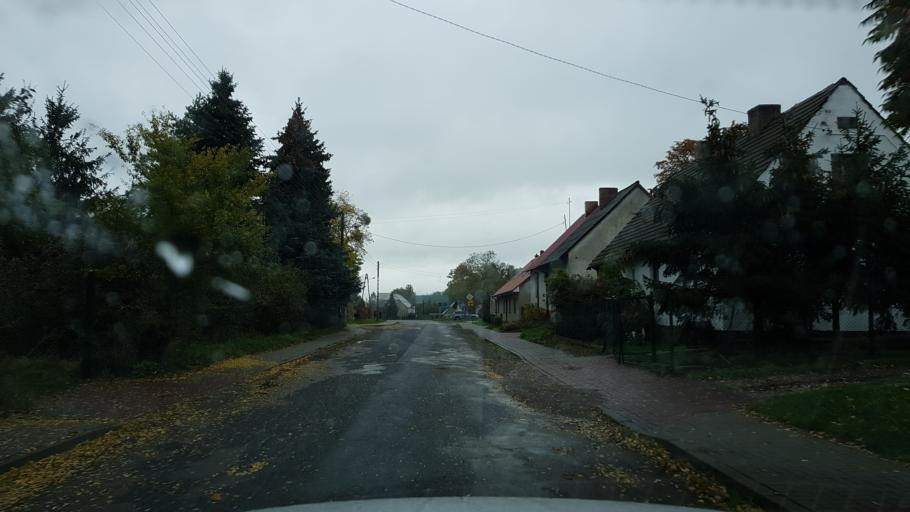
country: PL
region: West Pomeranian Voivodeship
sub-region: Powiat pyrzycki
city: Kozielice
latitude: 53.0311
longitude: 14.8516
